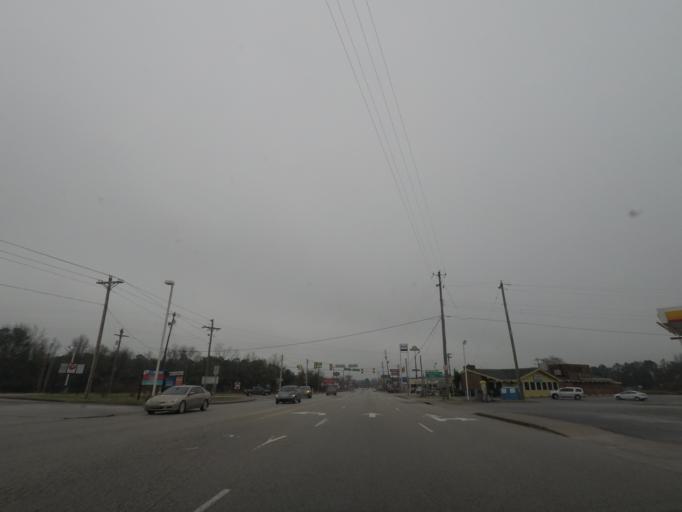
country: US
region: South Carolina
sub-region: Clarendon County
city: Manning
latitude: 33.7034
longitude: -80.2419
